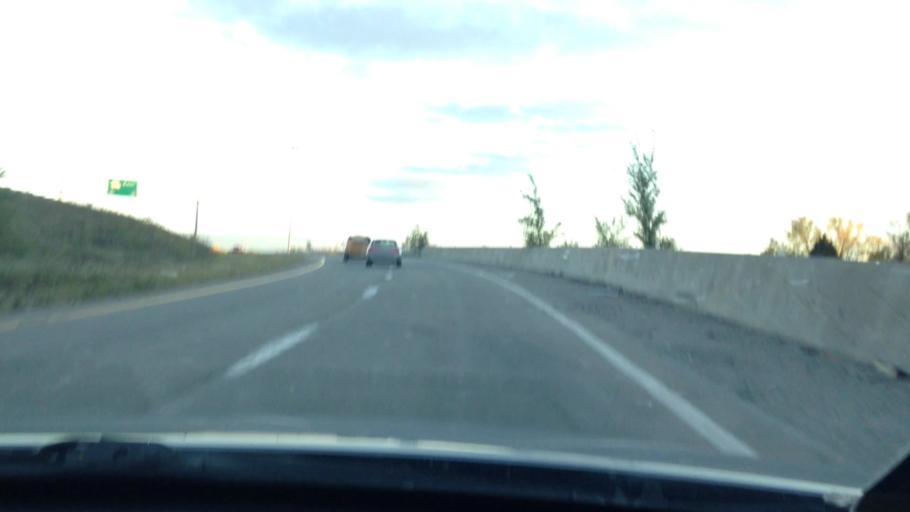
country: US
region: Missouri
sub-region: Jackson County
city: Raytown
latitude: 39.0189
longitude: -94.5005
